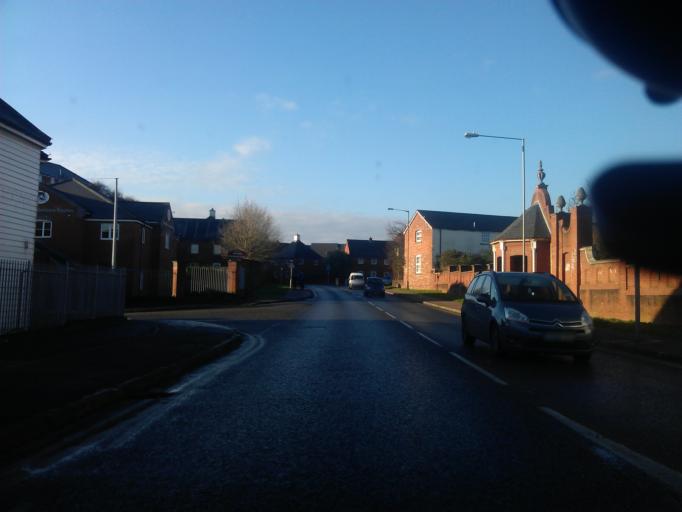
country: GB
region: England
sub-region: Essex
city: Colchester
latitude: 51.8837
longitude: 0.9260
